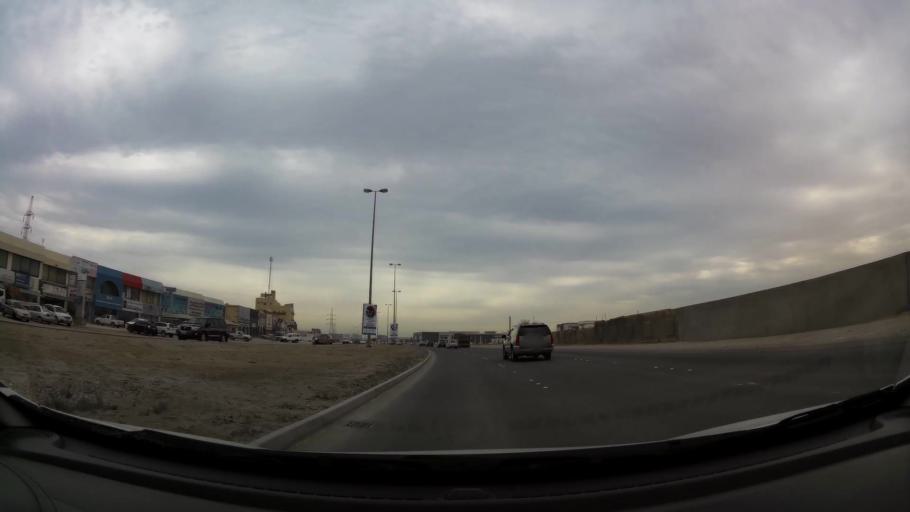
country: BH
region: Northern
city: Sitrah
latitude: 26.1575
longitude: 50.6065
